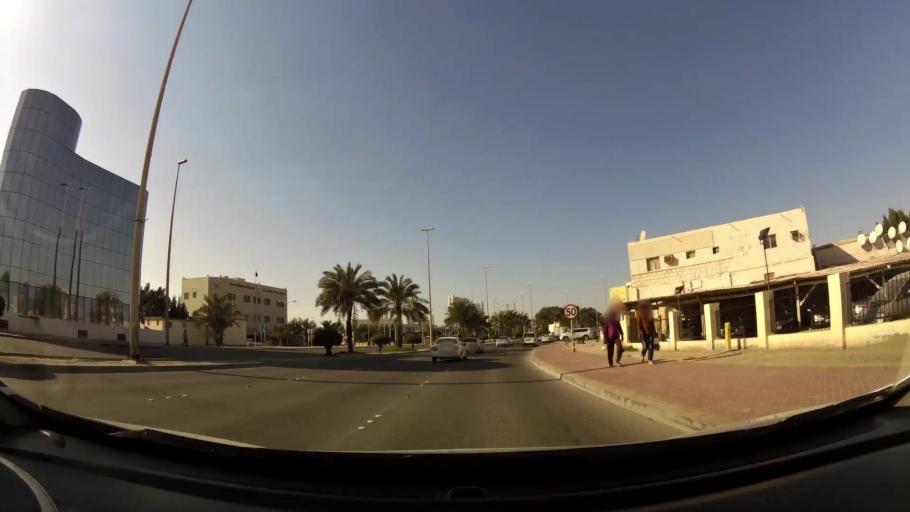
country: BH
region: Manama
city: Manama
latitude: 26.2148
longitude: 50.5655
